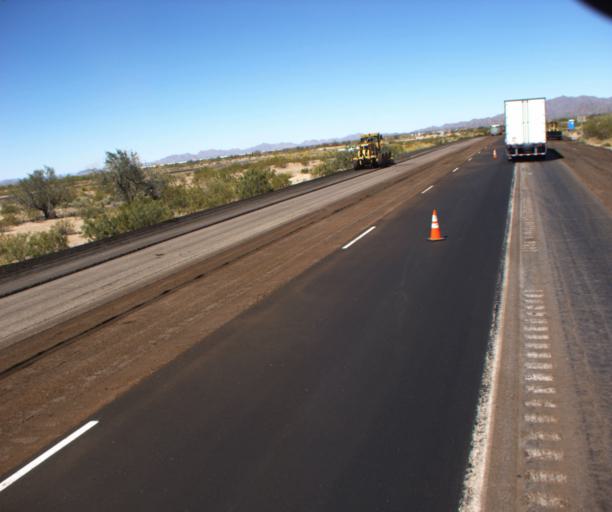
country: US
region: Arizona
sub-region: Maricopa County
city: Gila Bend
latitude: 33.0421
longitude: -112.6446
